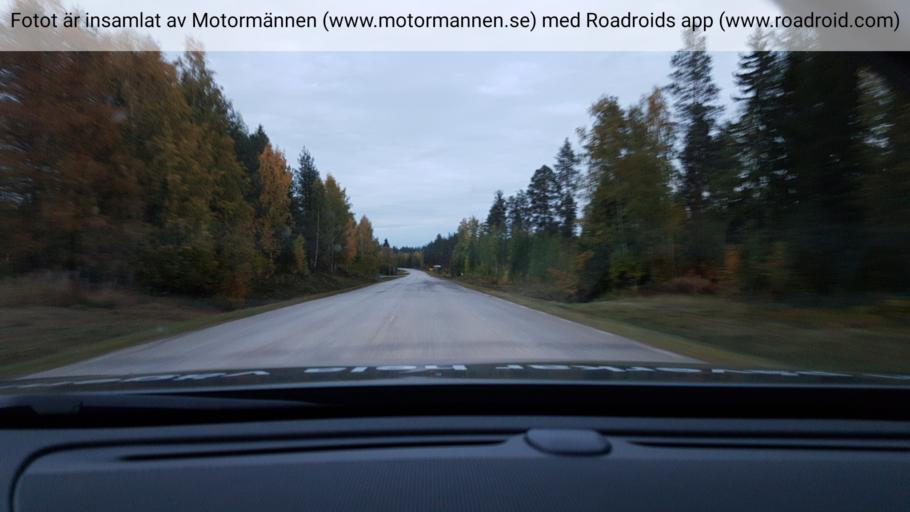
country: SE
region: Norrbotten
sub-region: Alvsbyns Kommun
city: AElvsbyn
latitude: 65.8406
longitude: 20.5070
